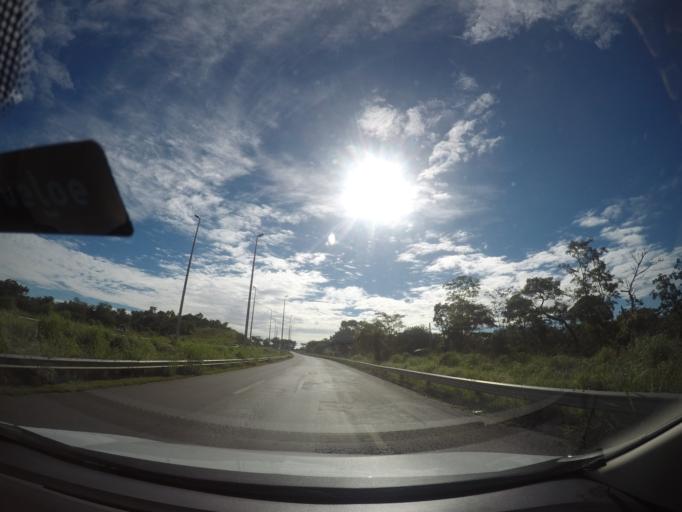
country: BR
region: Goias
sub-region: Senador Canedo
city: Senador Canedo
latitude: -16.6899
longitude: -49.1692
